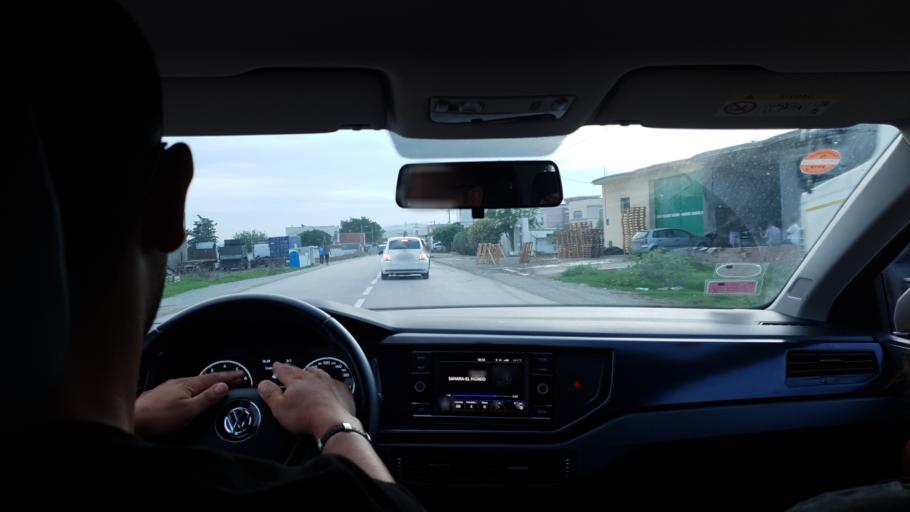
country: TN
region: Banzart
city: Al `Aliyah
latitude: 37.1297
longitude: 10.0644
